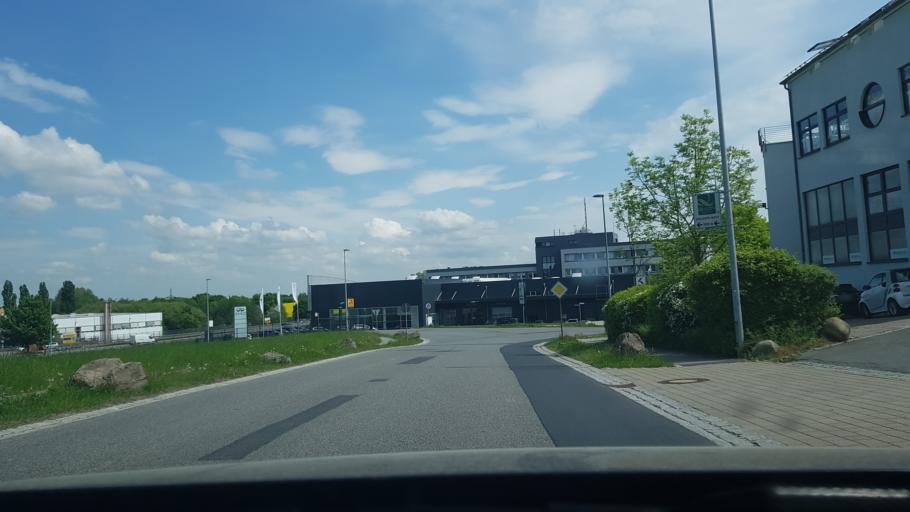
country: DE
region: Saxony
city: Tharandt
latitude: 51.0364
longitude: 13.5962
